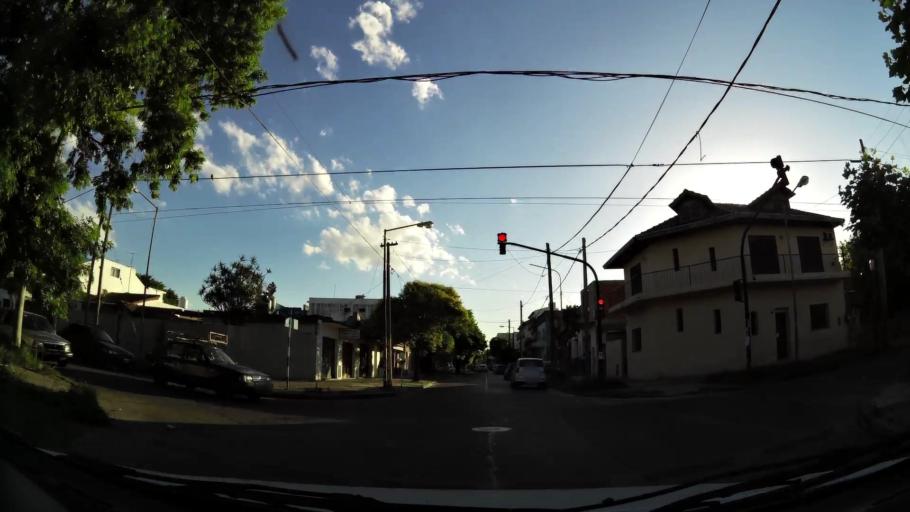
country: AR
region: Buenos Aires
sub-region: Partido de General San Martin
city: General San Martin
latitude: -34.5566
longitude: -58.5414
